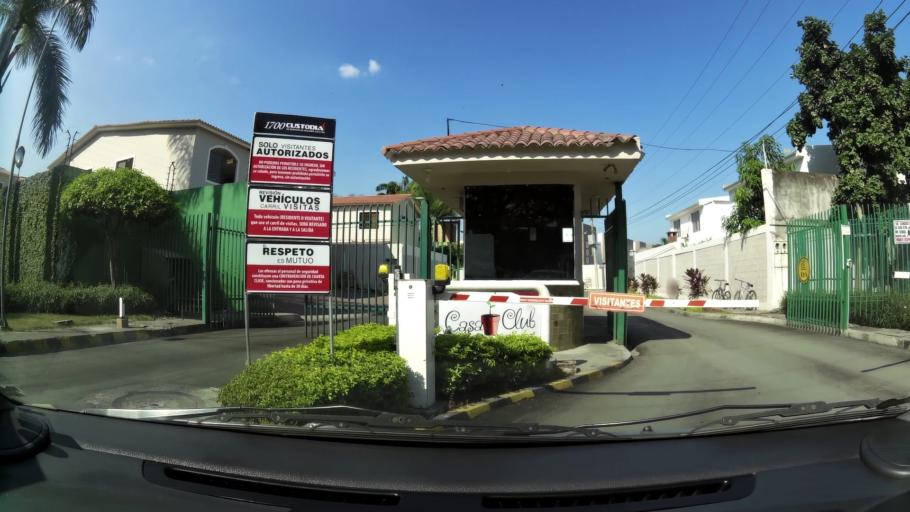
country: EC
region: Guayas
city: Santa Lucia
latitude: -2.1813
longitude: -79.9873
